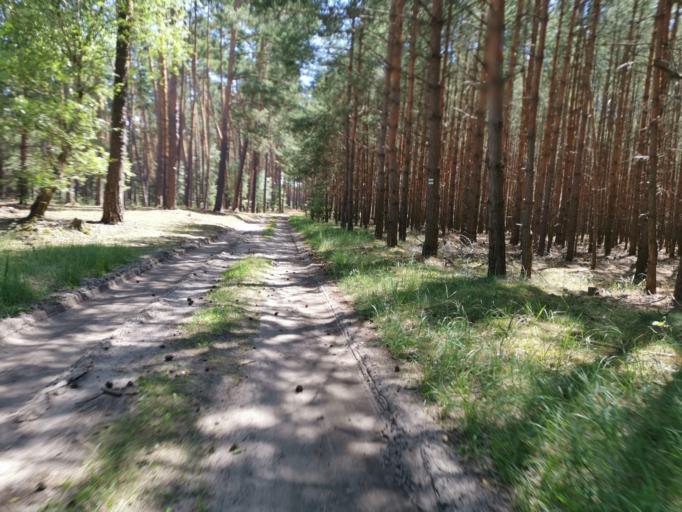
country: CZ
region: South Moravian
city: Vracov
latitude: 48.9664
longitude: 17.2207
